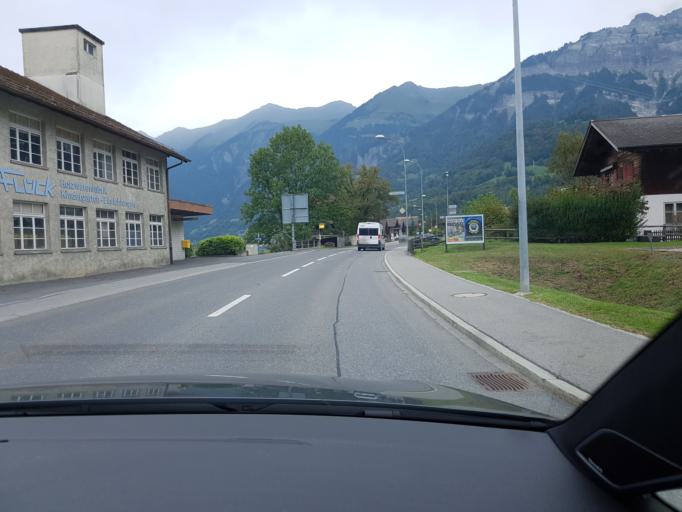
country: CH
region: Bern
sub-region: Interlaken-Oberhasli District
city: Brienz
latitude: 46.7459
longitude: 8.0573
